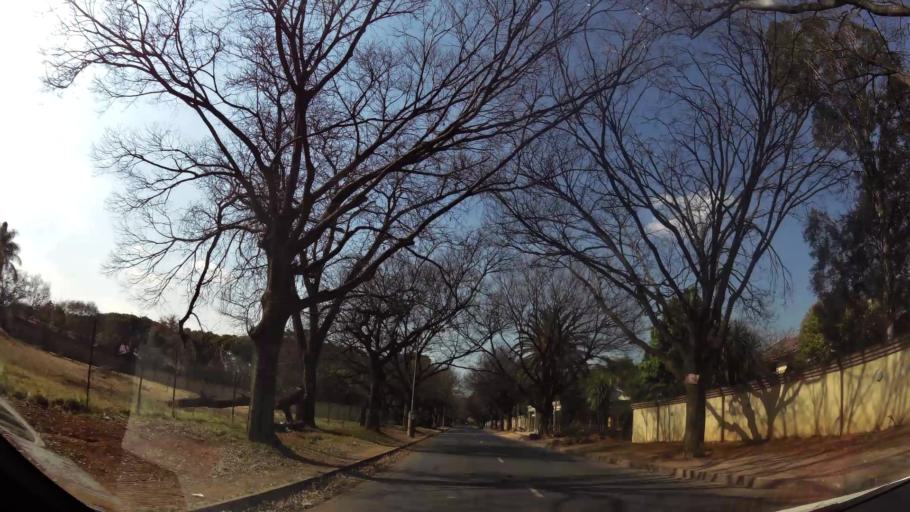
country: ZA
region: Gauteng
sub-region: Ekurhuleni Metropolitan Municipality
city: Benoni
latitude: -26.1850
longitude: 28.2851
